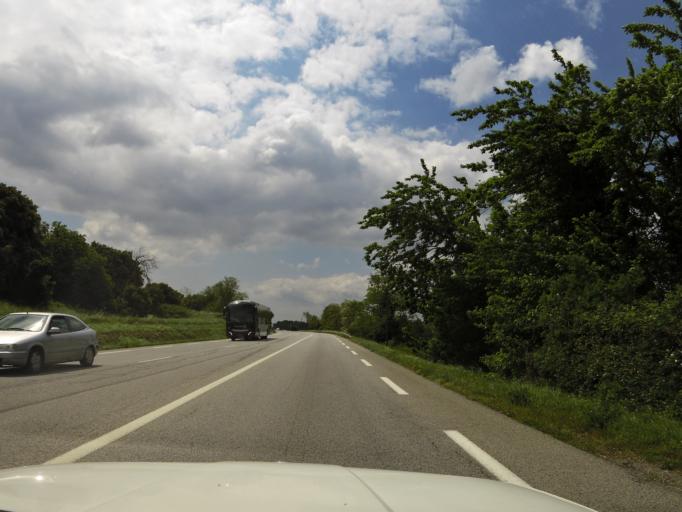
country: FR
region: Rhone-Alpes
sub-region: Departement de la Drome
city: Savasse
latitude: 44.6181
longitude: 4.7586
